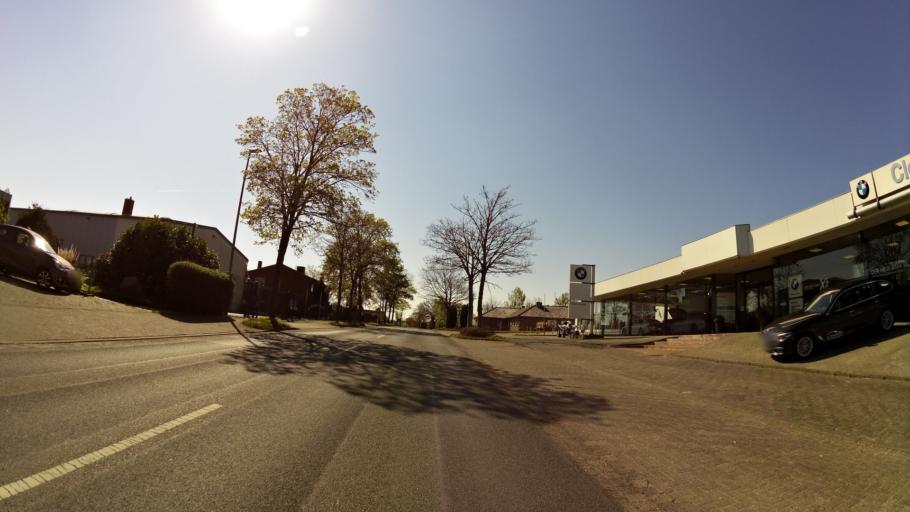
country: DE
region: Lower Saxony
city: Syke
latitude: 52.9171
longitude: 8.8013
